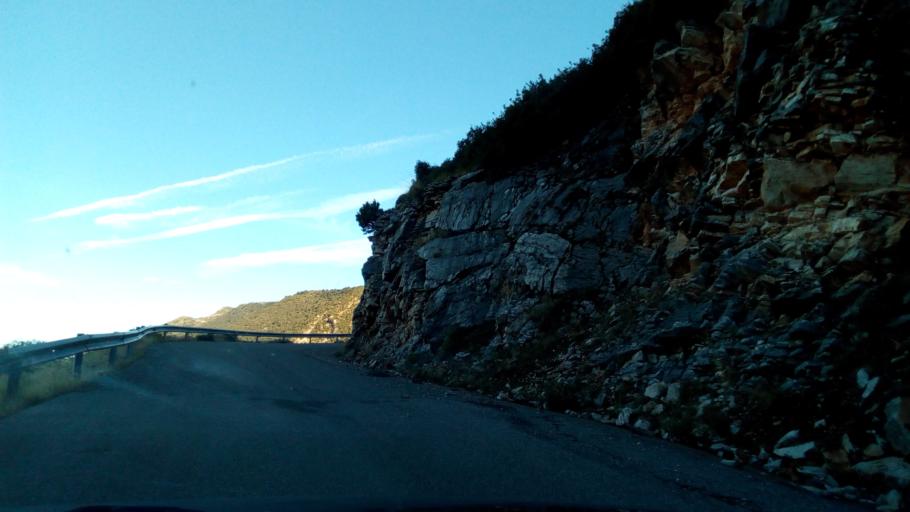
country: GR
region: West Greece
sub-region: Nomos Aitolias kai Akarnanias
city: Nafpaktos
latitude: 38.5149
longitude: 21.8471
